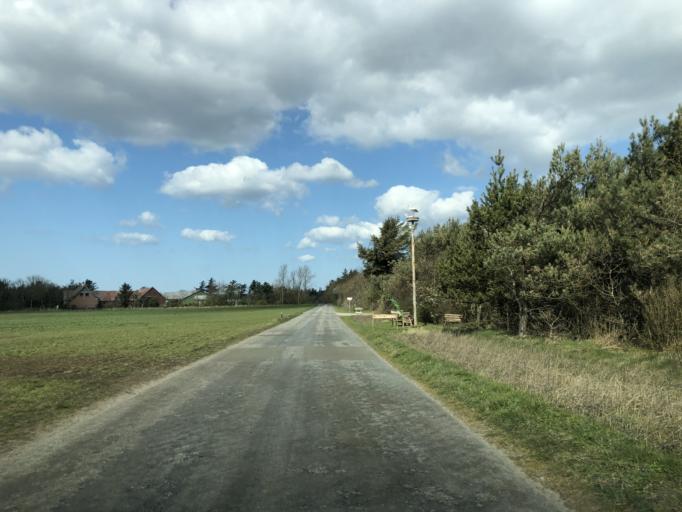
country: DK
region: Central Jutland
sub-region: Holstebro Kommune
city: Ulfborg
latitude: 56.3759
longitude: 8.2101
